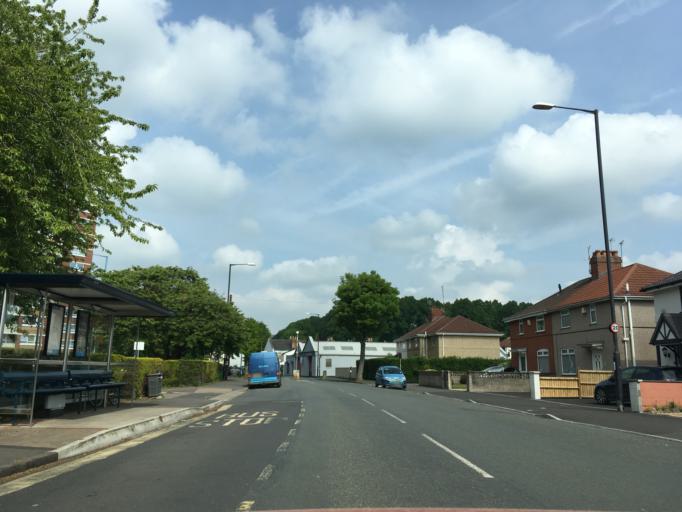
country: GB
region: England
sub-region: Bristol
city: Bristol
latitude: 51.4404
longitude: -2.6169
